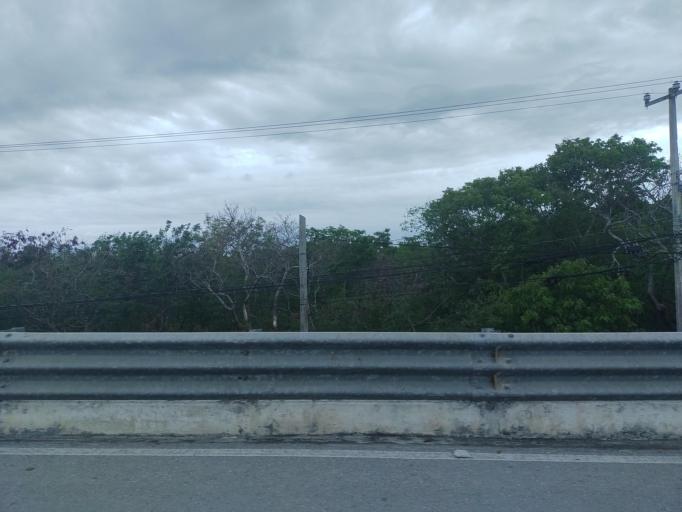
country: MX
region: Quintana Roo
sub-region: Tulum
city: Ciudad Chemuyil
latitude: 20.3998
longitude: -87.3198
